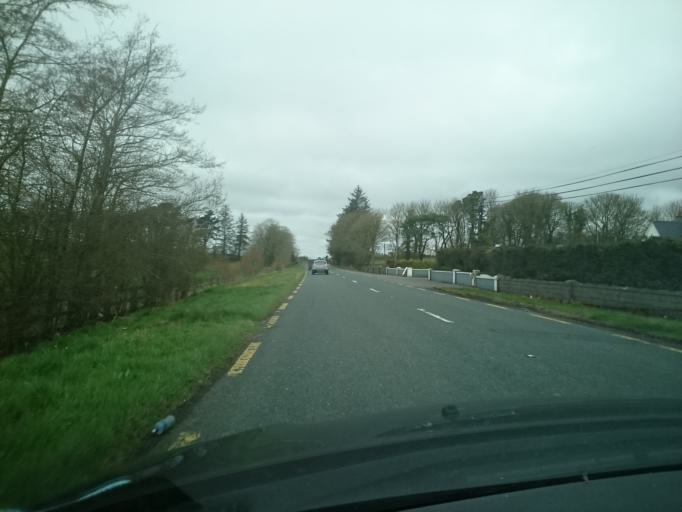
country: IE
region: Connaught
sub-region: Maigh Eo
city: Claremorris
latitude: 53.7771
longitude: -9.0718
